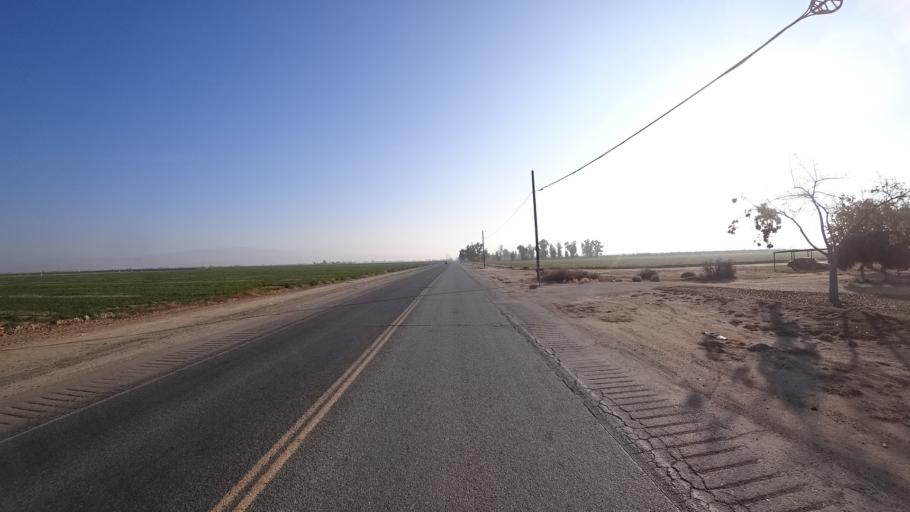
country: US
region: California
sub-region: Kern County
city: Lamont
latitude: 35.2669
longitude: -118.9493
